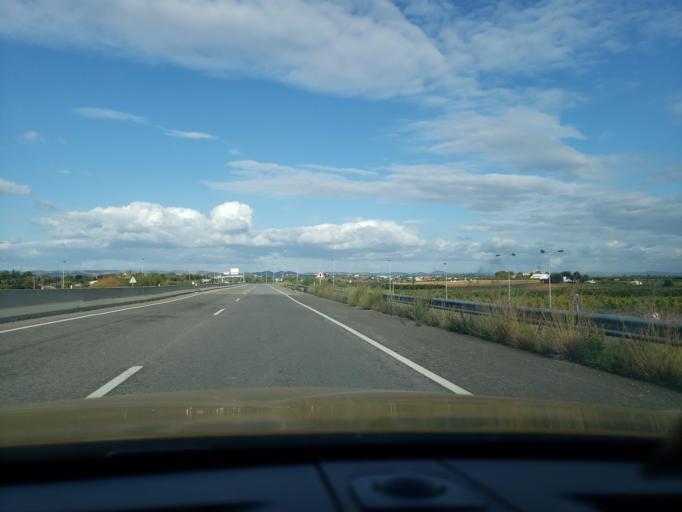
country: PT
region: Faro
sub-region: Lagoa
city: Lagoa
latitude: 37.1596
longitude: -8.4471
